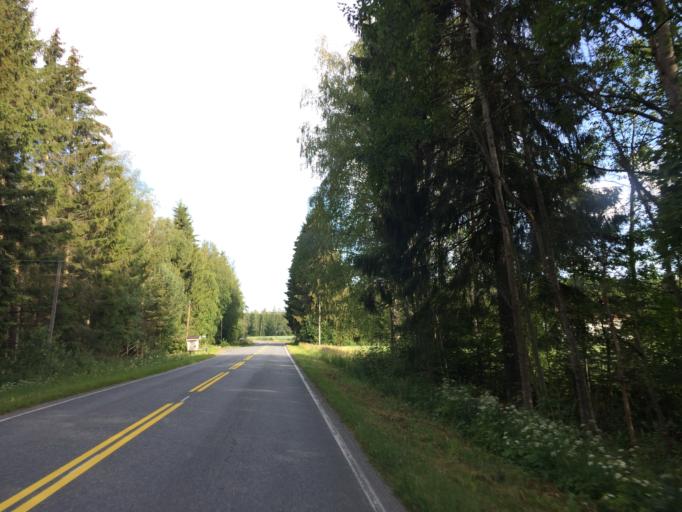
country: FI
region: Haeme
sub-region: Haemeenlinna
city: Janakkala
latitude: 60.9383
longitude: 24.5315
